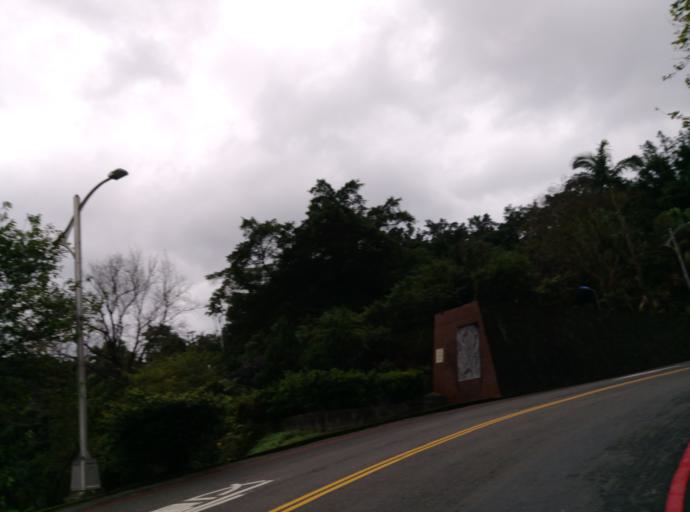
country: TW
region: Taiwan
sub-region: Keelung
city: Keelung
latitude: 25.1314
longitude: 121.7487
